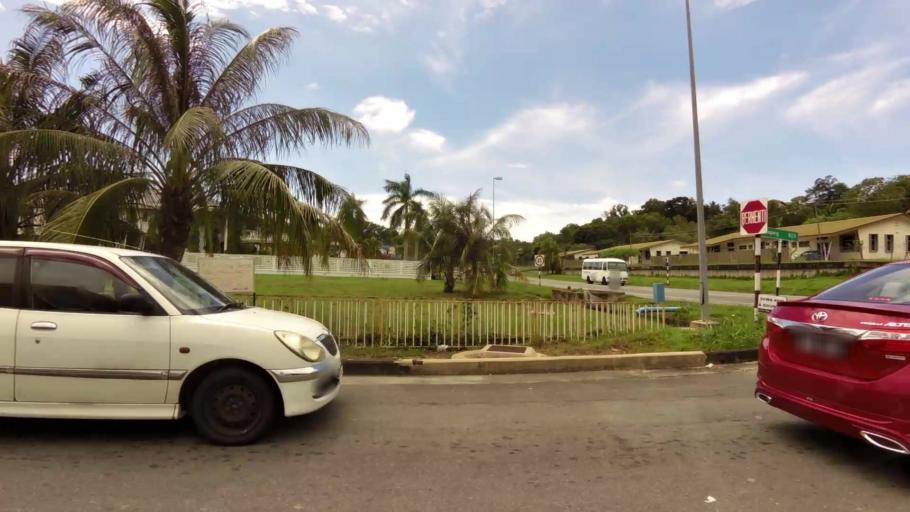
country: BN
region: Brunei and Muara
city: Bandar Seri Begawan
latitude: 4.9923
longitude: 114.9482
